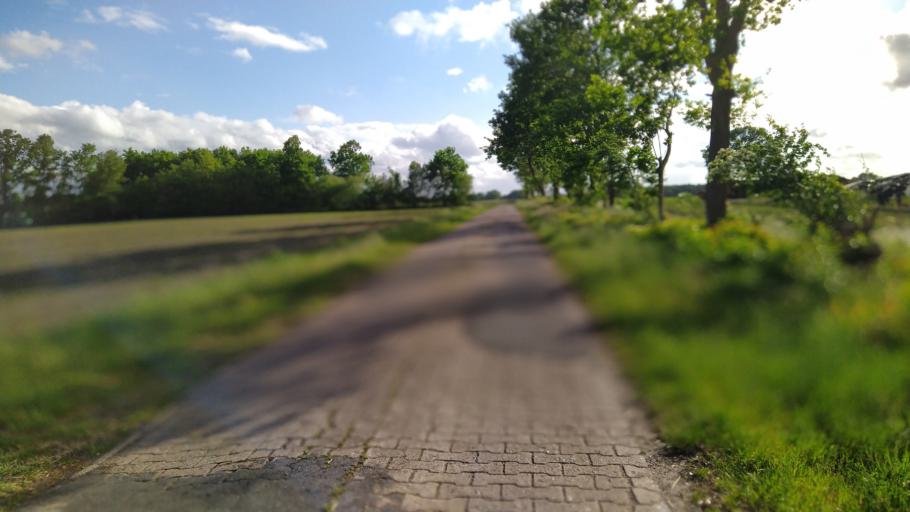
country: DE
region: Lower Saxony
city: Farven
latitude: 53.4442
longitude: 9.3143
